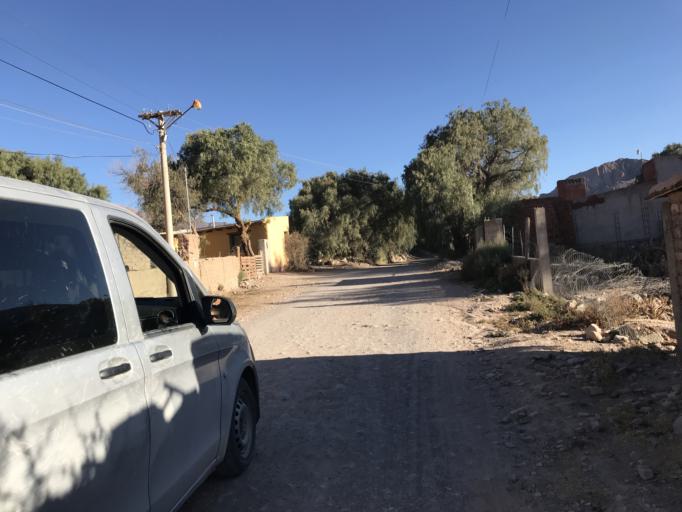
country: AR
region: Jujuy
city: Maimara
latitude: -23.5785
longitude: -65.4014
